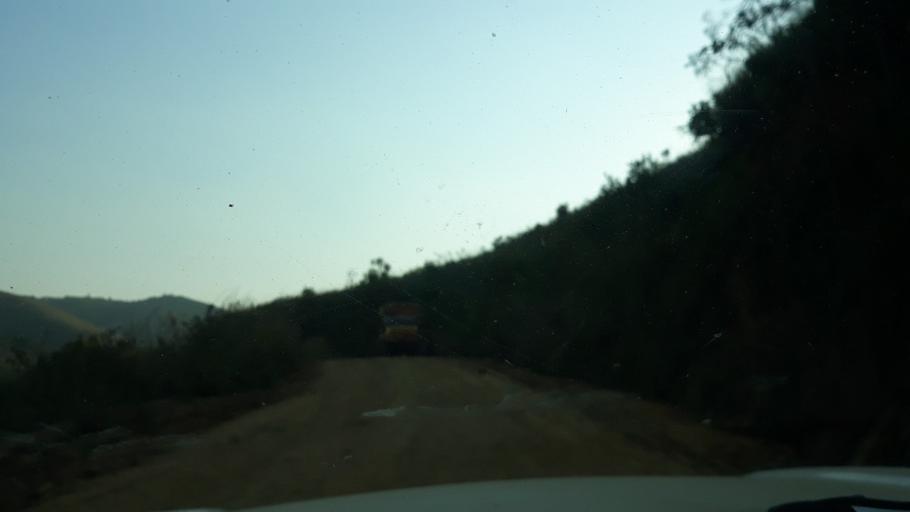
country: RW
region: Western Province
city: Cyangugu
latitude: -2.7039
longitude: 28.9237
